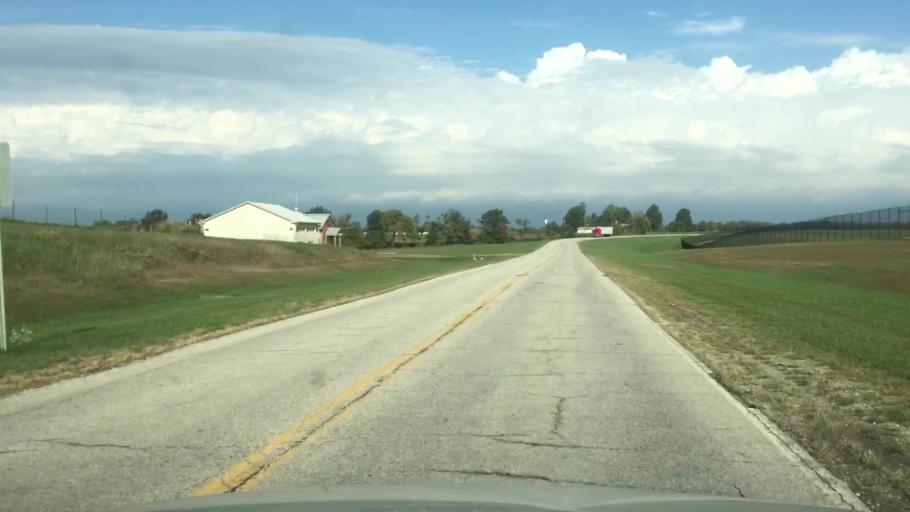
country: US
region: Missouri
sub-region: Boone County
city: Ashland
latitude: 38.8245
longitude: -92.2236
